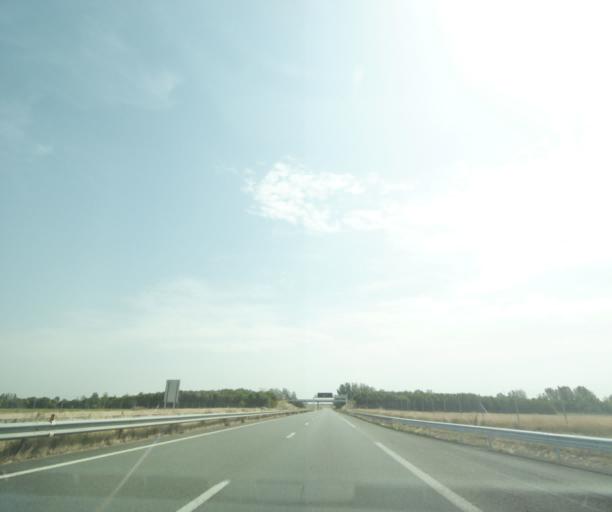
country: FR
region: Pays de la Loire
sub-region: Departement de la Vendee
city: Maillezais
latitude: 46.3976
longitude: -0.6801
